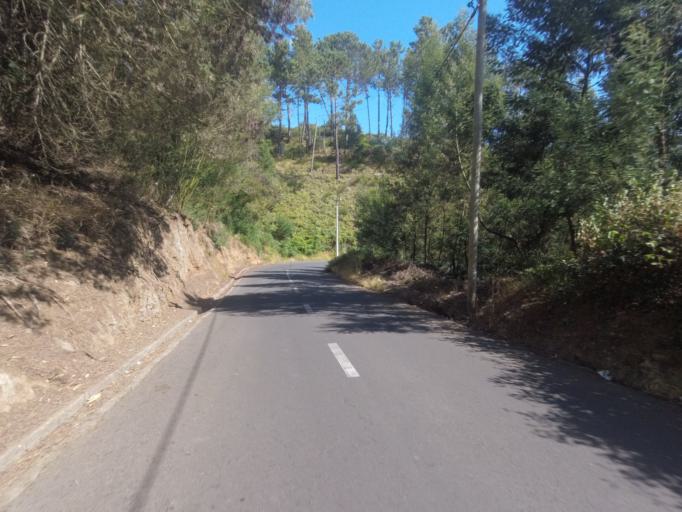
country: PT
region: Madeira
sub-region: Ribeira Brava
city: Campanario
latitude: 32.6939
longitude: -17.0312
